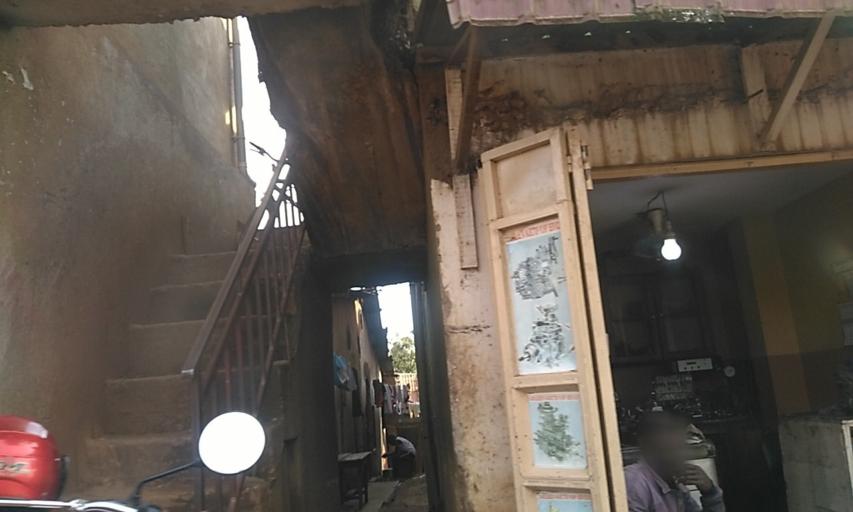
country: UG
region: Central Region
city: Kampala Central Division
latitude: 0.3236
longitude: 32.5701
